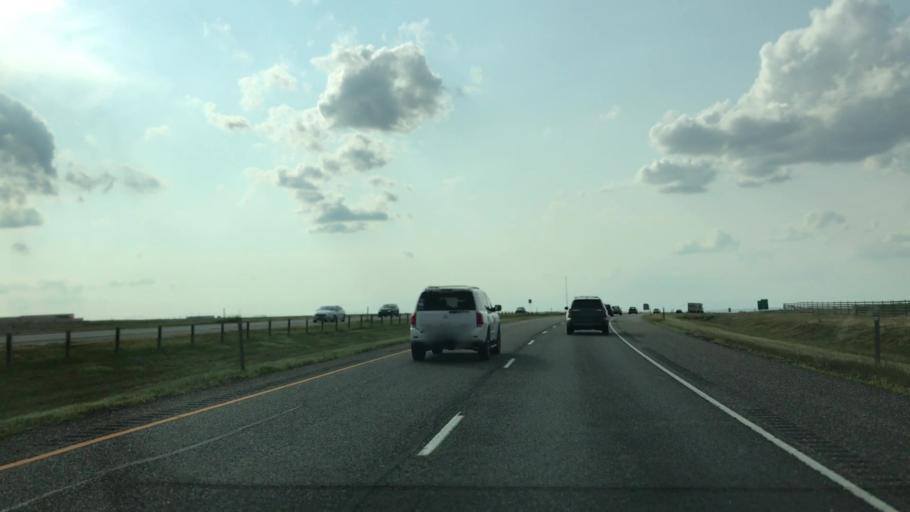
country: US
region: Colorado
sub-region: Adams County
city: Aurora
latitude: 39.8190
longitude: -104.7403
